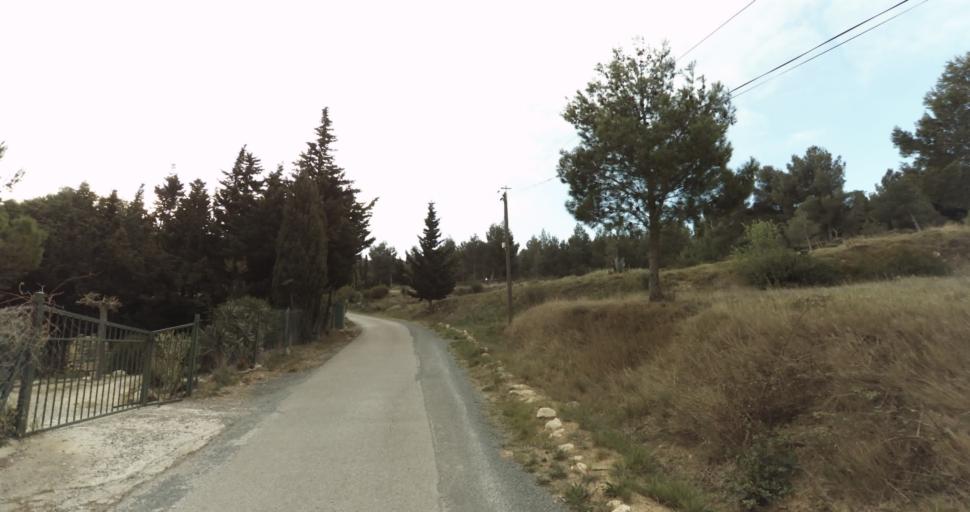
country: FR
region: Languedoc-Roussillon
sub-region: Departement de l'Aude
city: Leucate
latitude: 42.9331
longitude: 3.0223
